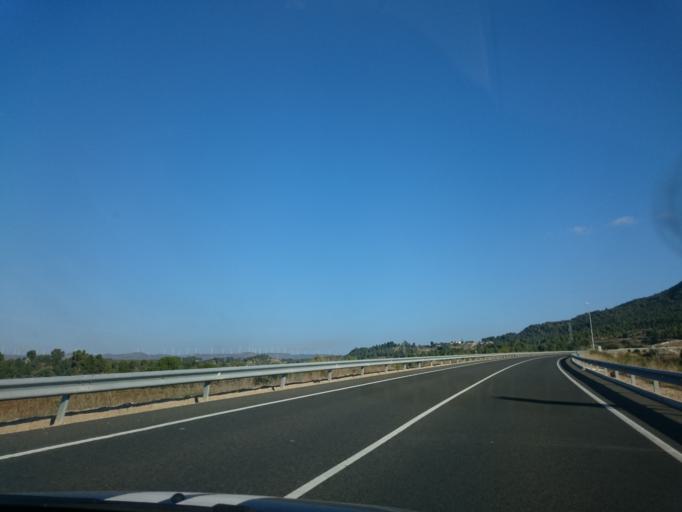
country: ES
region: Catalonia
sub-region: Provincia de Barcelona
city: Odena
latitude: 41.5945
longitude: 1.6622
